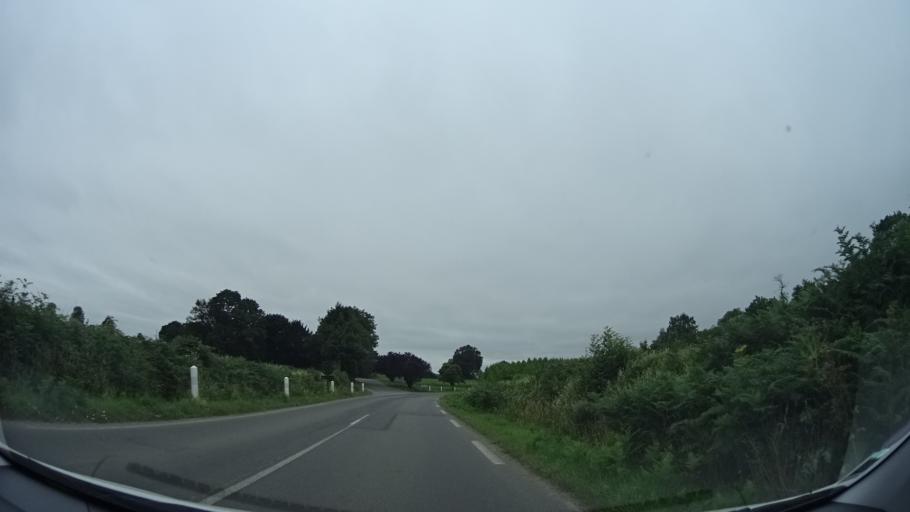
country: FR
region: Brittany
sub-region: Departement d'Ille-et-Vilaine
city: Irodouer
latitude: 48.3025
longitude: -1.9417
